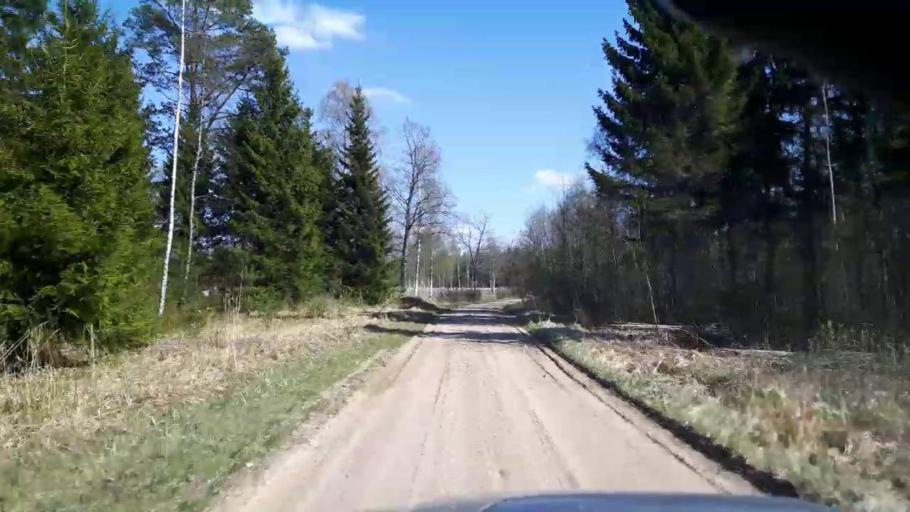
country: EE
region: Paernumaa
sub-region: Tootsi vald
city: Tootsi
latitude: 58.5416
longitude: 24.8097
